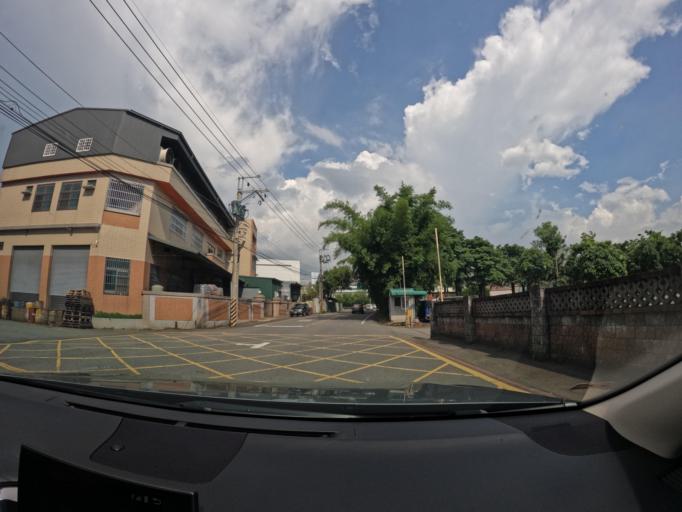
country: TW
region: Taiwan
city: Fengyuan
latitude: 24.2951
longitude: 120.7227
